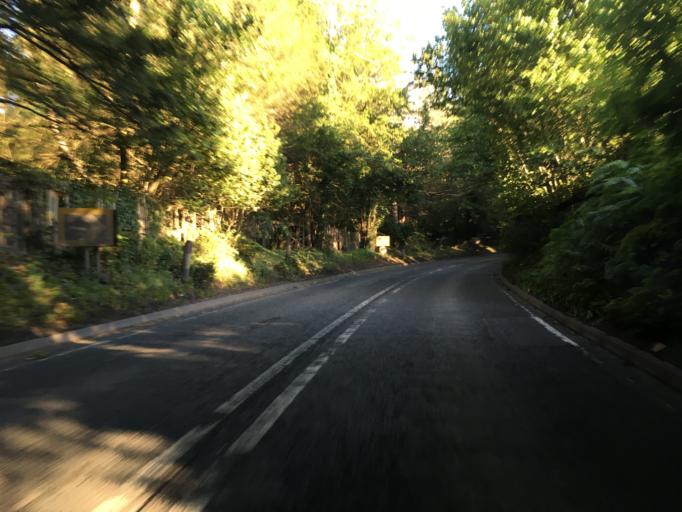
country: GB
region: England
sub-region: Hampshire
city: Tadley
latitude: 51.3756
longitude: -1.1508
